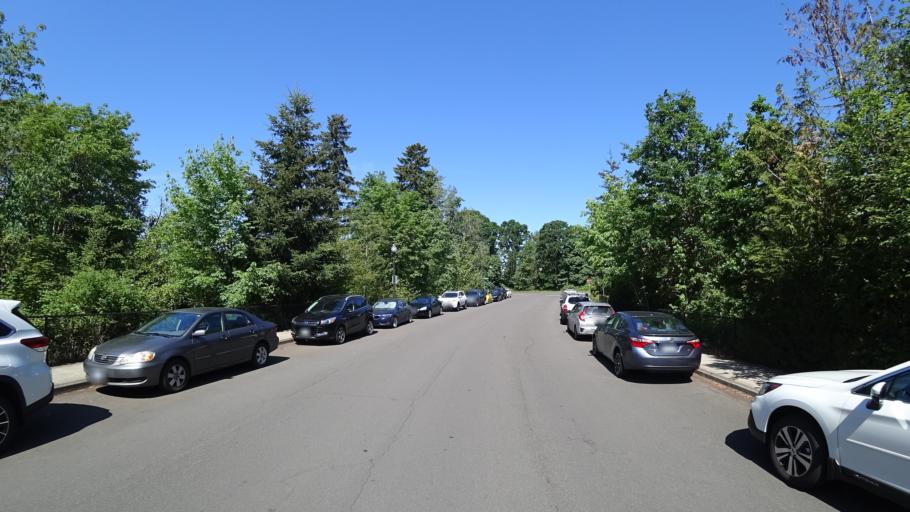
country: US
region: Oregon
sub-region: Washington County
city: Rockcreek
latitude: 45.5293
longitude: -122.9251
